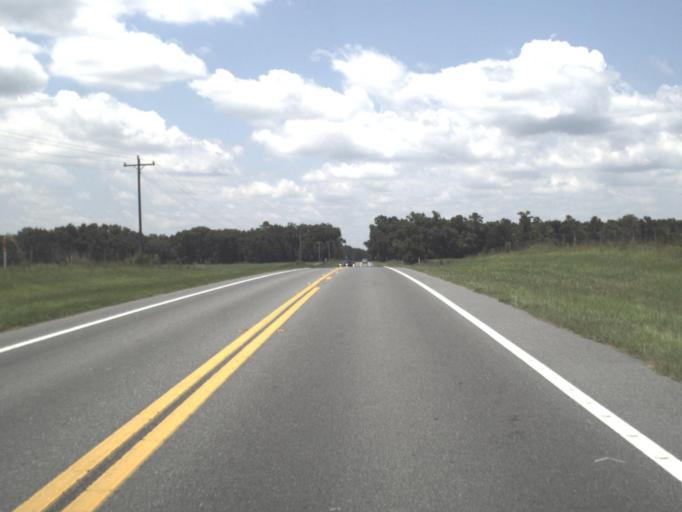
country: US
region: Florida
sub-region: Levy County
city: Williston
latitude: 29.4682
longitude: -82.4149
